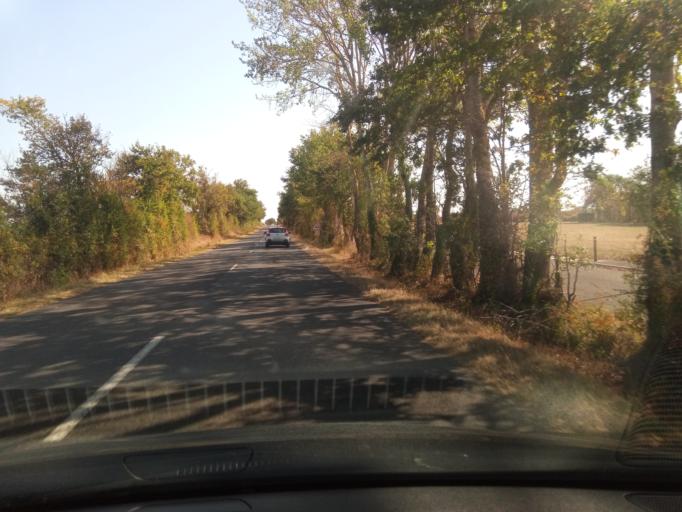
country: FR
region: Poitou-Charentes
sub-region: Departement de la Vienne
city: Montmorillon
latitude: 46.4337
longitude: 0.9026
